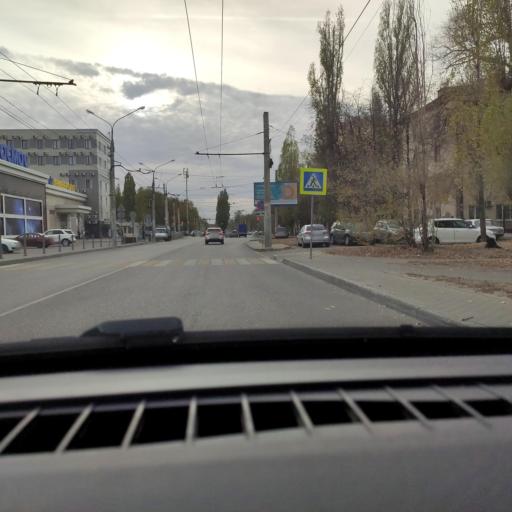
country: RU
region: Voronezj
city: Voronezh
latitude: 51.6619
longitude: 39.1551
